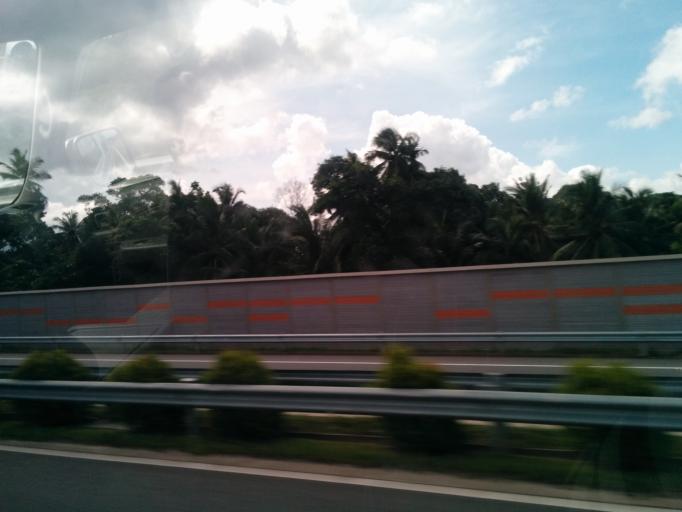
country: LK
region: Western
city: Wattala
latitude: 6.9745
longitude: 79.8947
